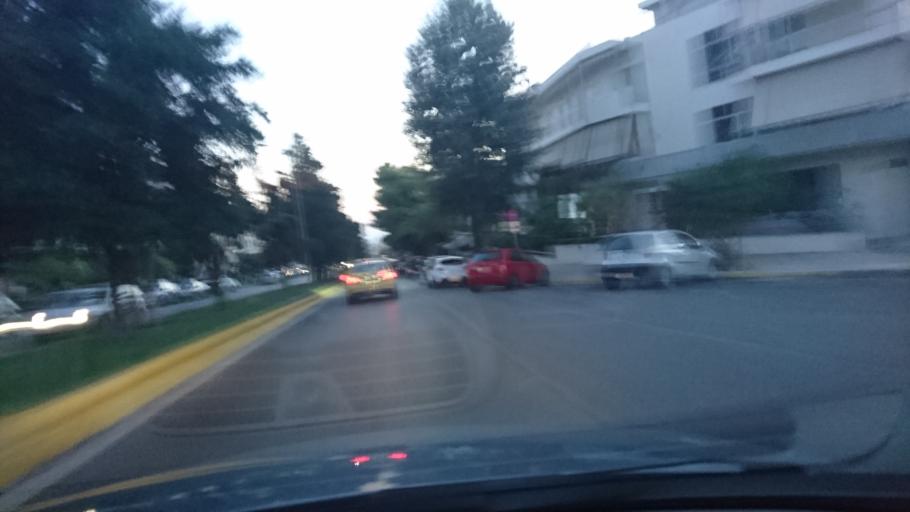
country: GR
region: Attica
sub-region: Nomarchia Athinas
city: Argyroupoli
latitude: 37.9175
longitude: 23.7472
